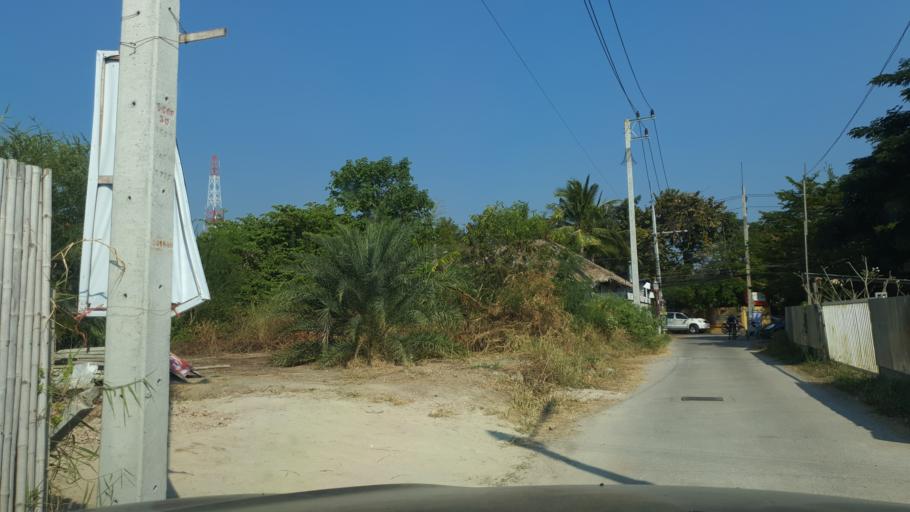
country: TH
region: Prachuap Khiri Khan
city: Hua Hin
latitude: 12.5539
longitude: 99.9551
